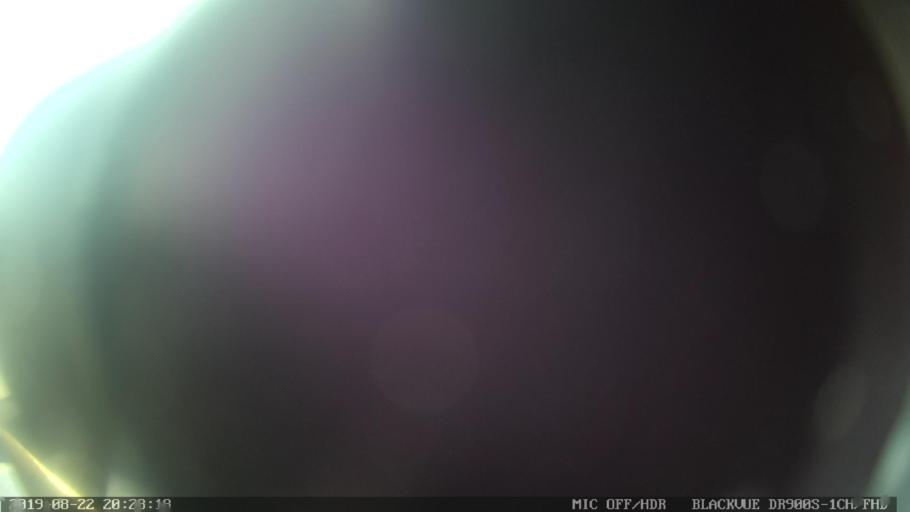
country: PT
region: Castelo Branco
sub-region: Castelo Branco
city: Castelo Branco
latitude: 39.7799
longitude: -7.5813
